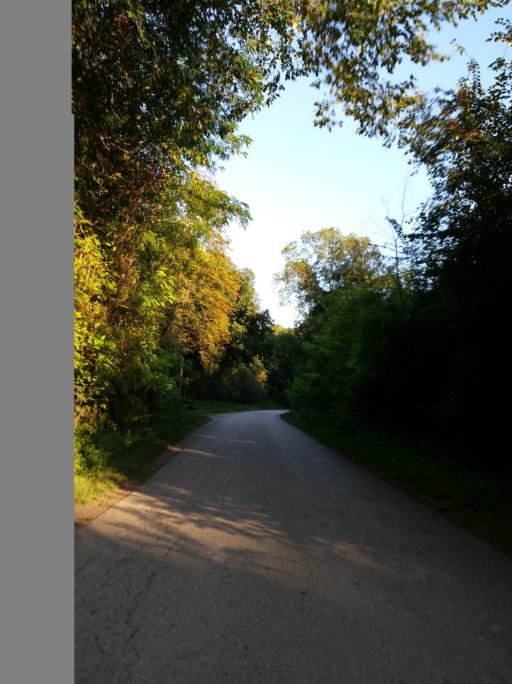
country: AT
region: Lower Austria
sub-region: Politischer Bezirk Ganserndorf
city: Gross-Enzersdorf
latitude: 48.1933
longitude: 16.4985
